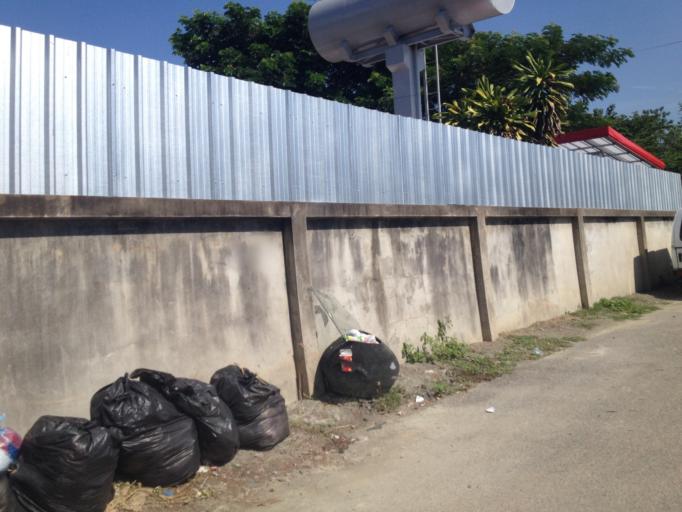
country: TH
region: Chiang Mai
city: Hang Dong
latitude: 18.6945
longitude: 98.9263
